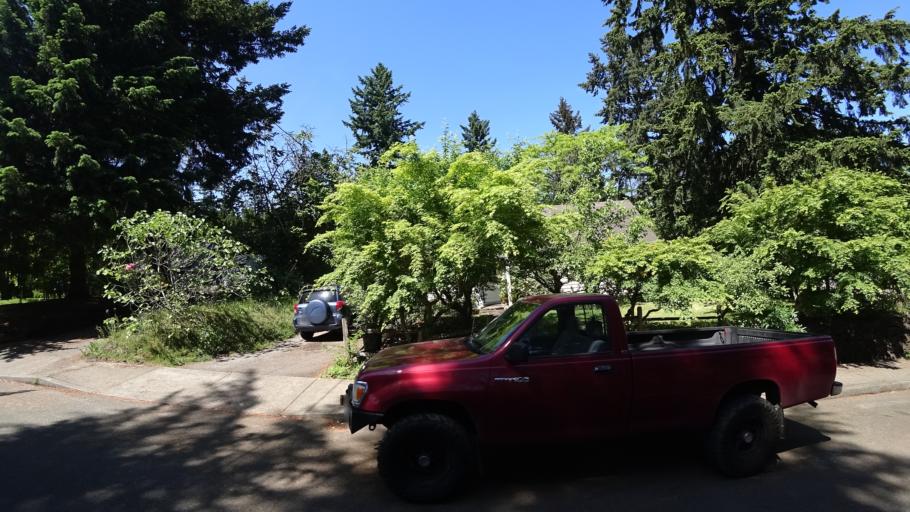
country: US
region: Oregon
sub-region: Washington County
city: Metzger
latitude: 45.4465
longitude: -122.7123
